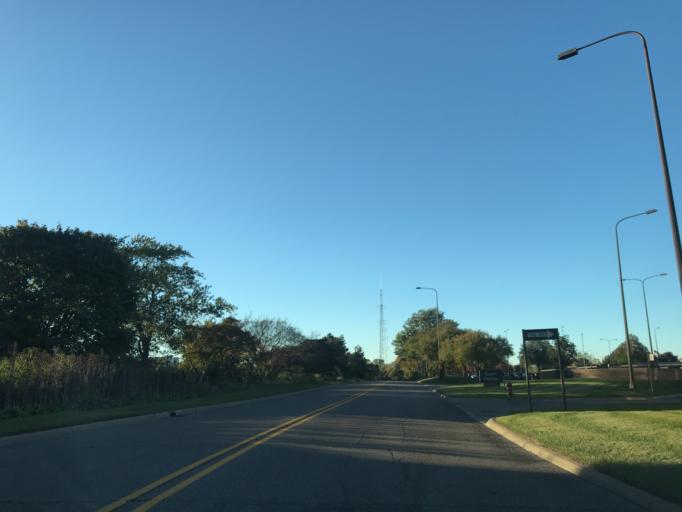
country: US
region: Michigan
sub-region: Oakland County
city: Clawson
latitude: 42.5631
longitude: -83.1555
